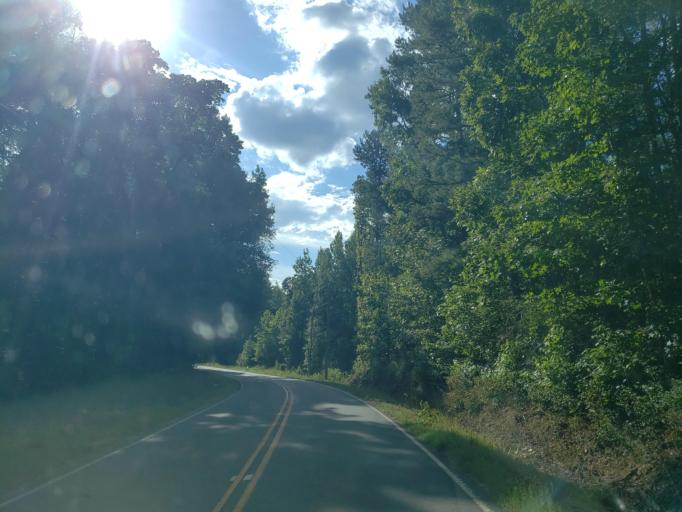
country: US
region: Georgia
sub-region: Floyd County
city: Lindale
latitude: 34.1900
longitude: -85.0584
